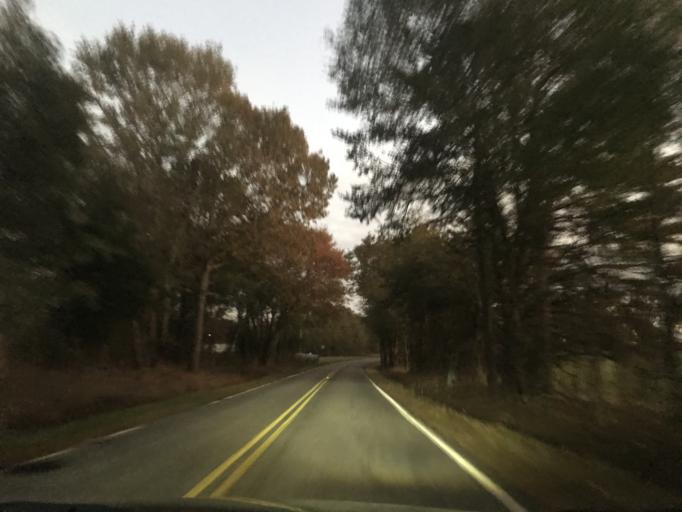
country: US
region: South Carolina
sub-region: Spartanburg County
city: Mayo
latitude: 35.0718
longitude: -81.9006
